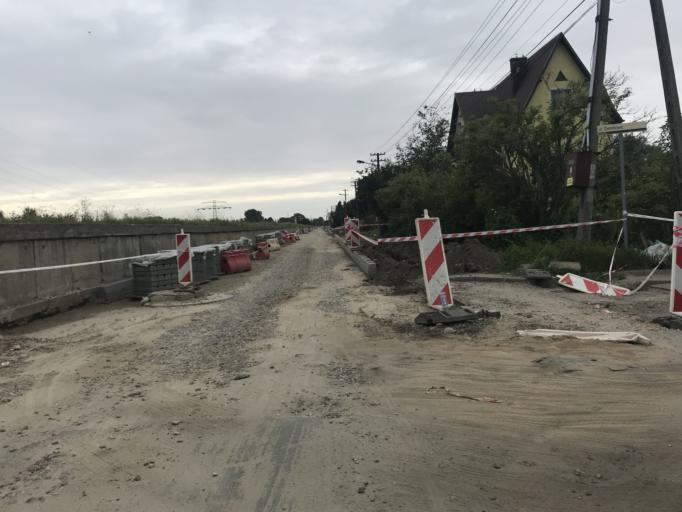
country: PL
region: Pomeranian Voivodeship
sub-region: Gdansk
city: Gdansk
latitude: 54.3442
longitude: 18.6815
